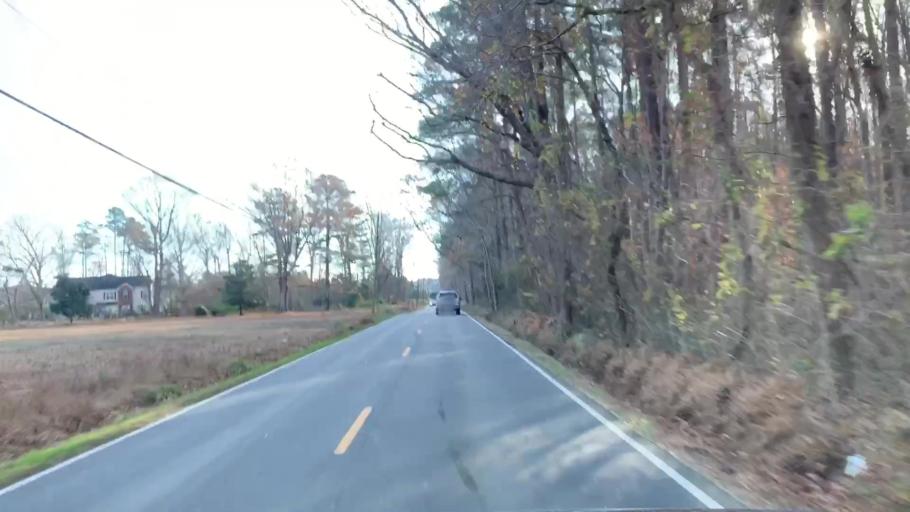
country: US
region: Virginia
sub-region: City of Virginia Beach
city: Virginia Beach
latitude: 36.7261
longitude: -76.0748
